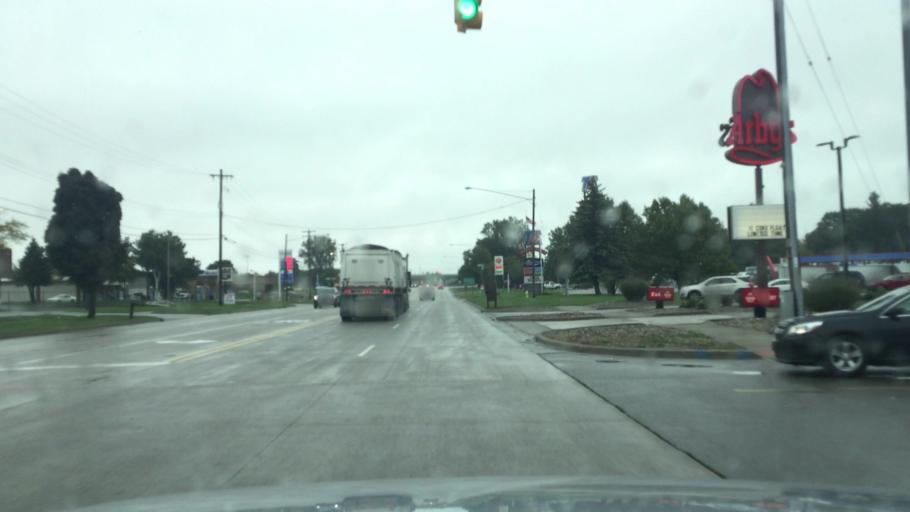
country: US
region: Michigan
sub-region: Saginaw County
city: Bridgeport
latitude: 43.3535
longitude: -83.8708
